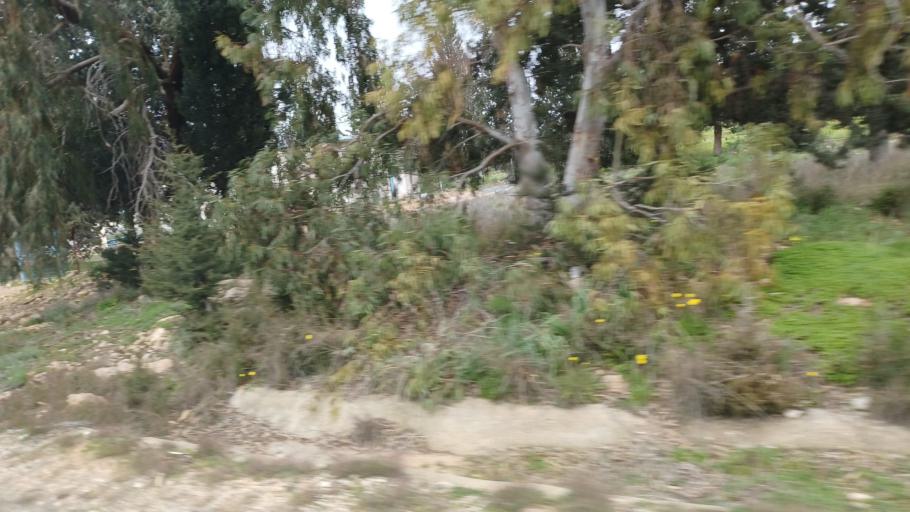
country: CY
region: Pafos
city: Paphos
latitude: 34.7715
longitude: 32.4581
